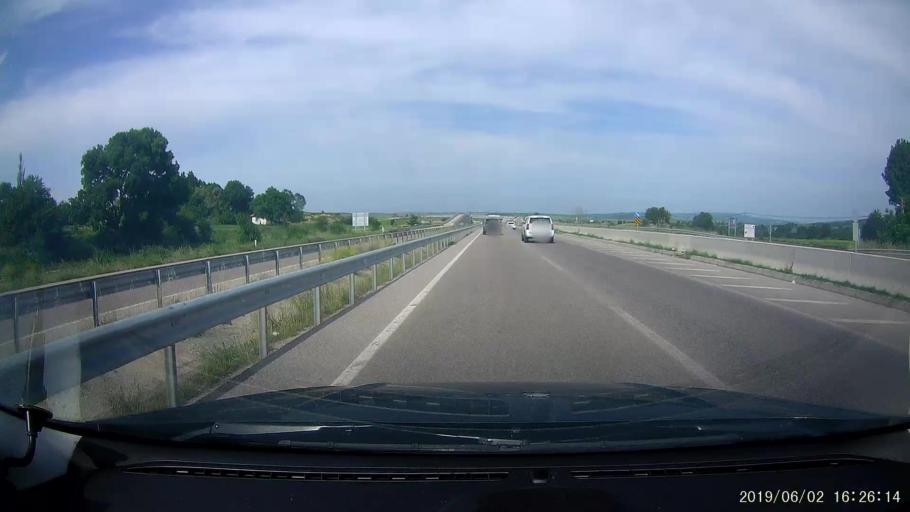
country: TR
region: Samsun
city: Ladik
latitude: 40.9986
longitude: 35.7971
